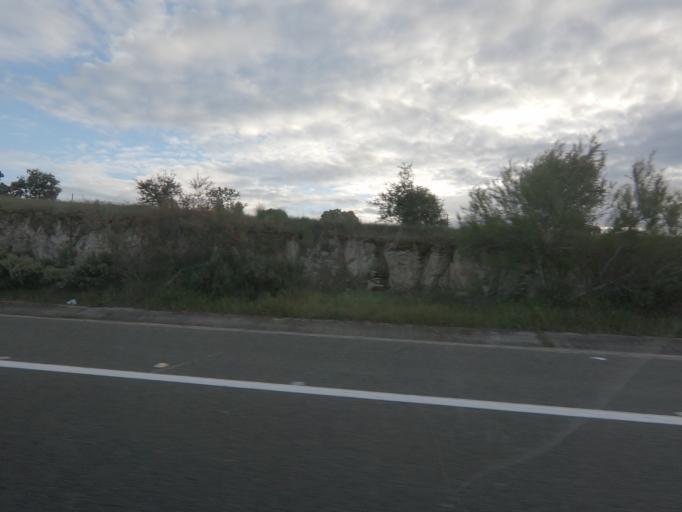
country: ES
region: Extremadura
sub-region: Provincia de Caceres
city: Caceres
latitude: 39.4560
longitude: -6.4193
